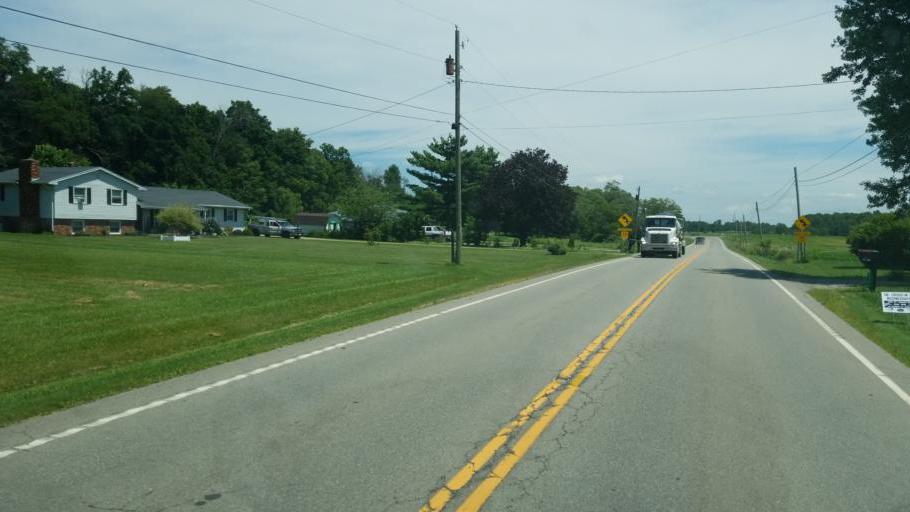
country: US
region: Ohio
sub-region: Richland County
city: Shelby
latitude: 40.8857
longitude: -82.5936
